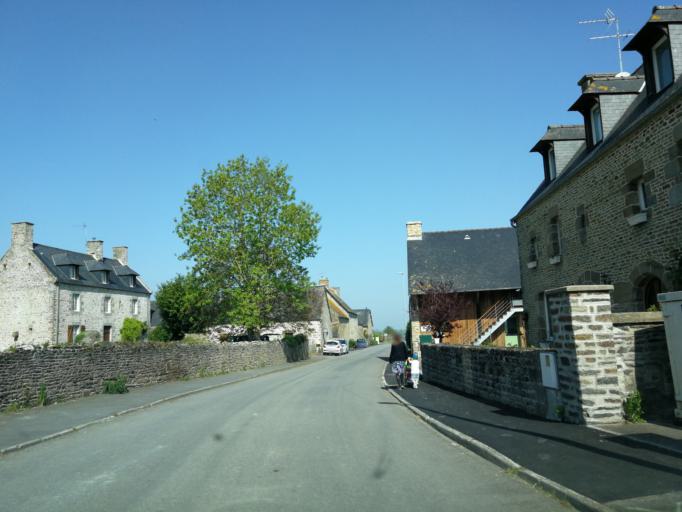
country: FR
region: Lower Normandy
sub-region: Departement de la Manche
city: Pontorson
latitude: 48.6029
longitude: -1.4752
